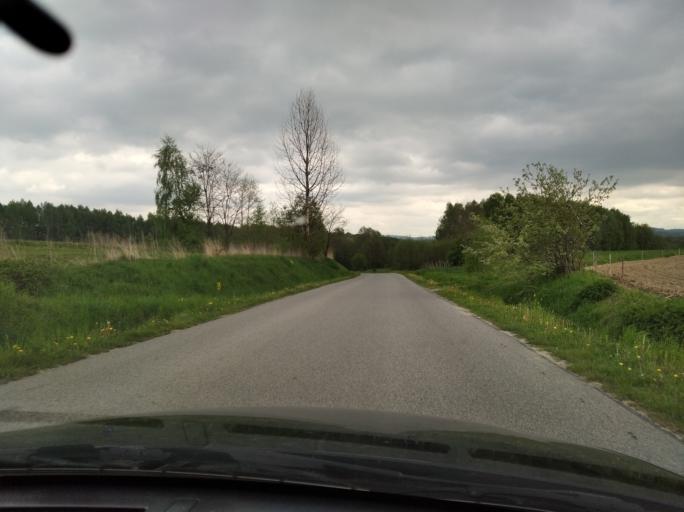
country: PL
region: Subcarpathian Voivodeship
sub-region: Powiat debicki
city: Leki Gorne
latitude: 49.9827
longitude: 21.1527
